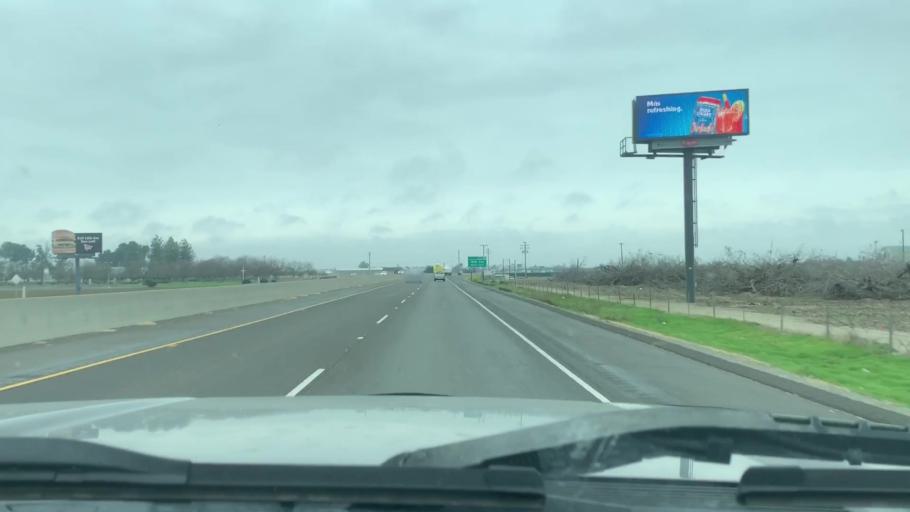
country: US
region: California
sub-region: Kings County
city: Armona
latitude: 36.3159
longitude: -119.6867
